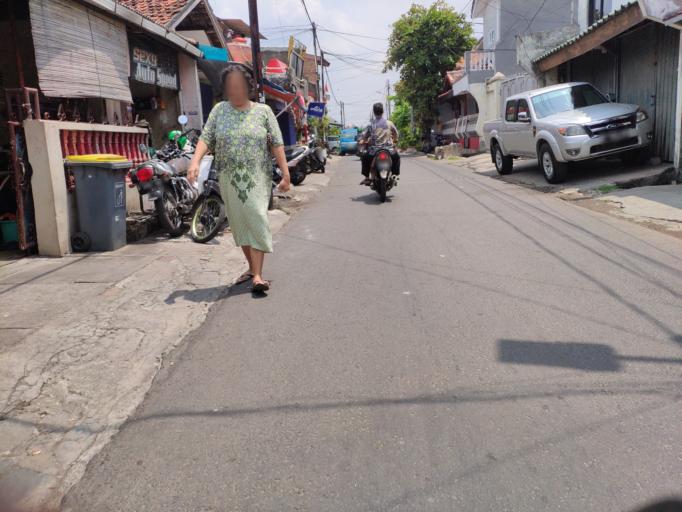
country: ID
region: Jakarta Raya
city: Jakarta
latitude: -6.2085
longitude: 106.8686
